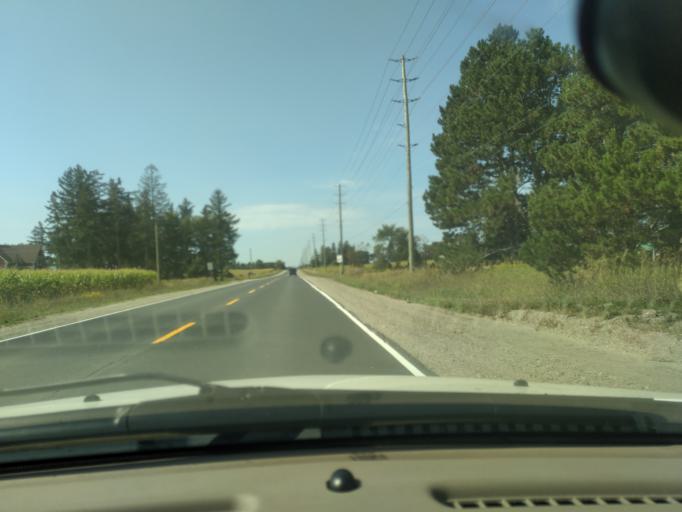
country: CA
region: Ontario
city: Innisfil
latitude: 44.2790
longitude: -79.7068
